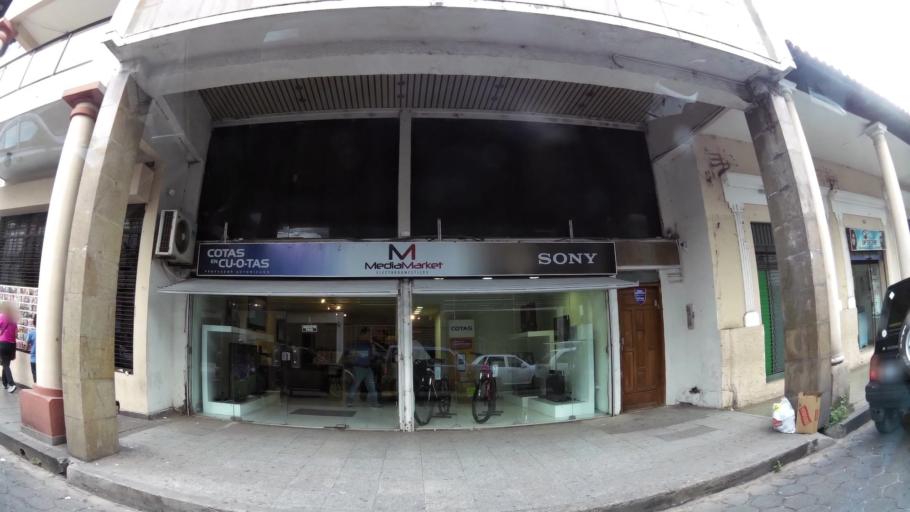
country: BO
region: Santa Cruz
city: Santa Cruz de la Sierra
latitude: -17.7826
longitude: -63.1792
